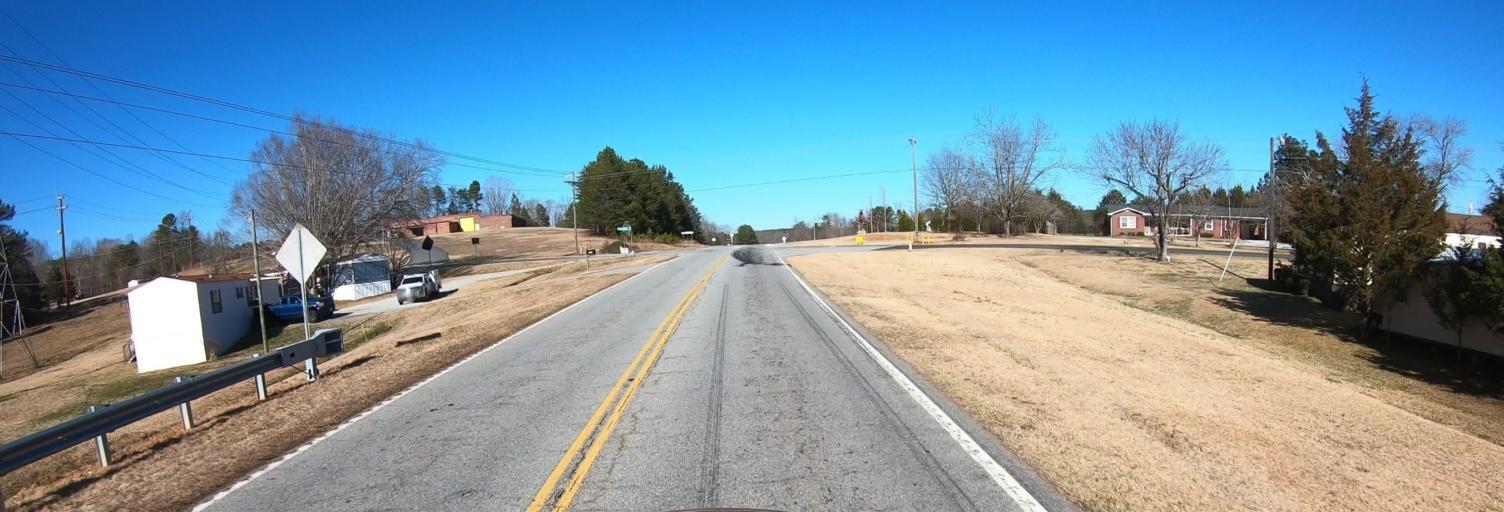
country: US
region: South Carolina
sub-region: Oconee County
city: Walhalla
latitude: 34.7381
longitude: -83.0530
